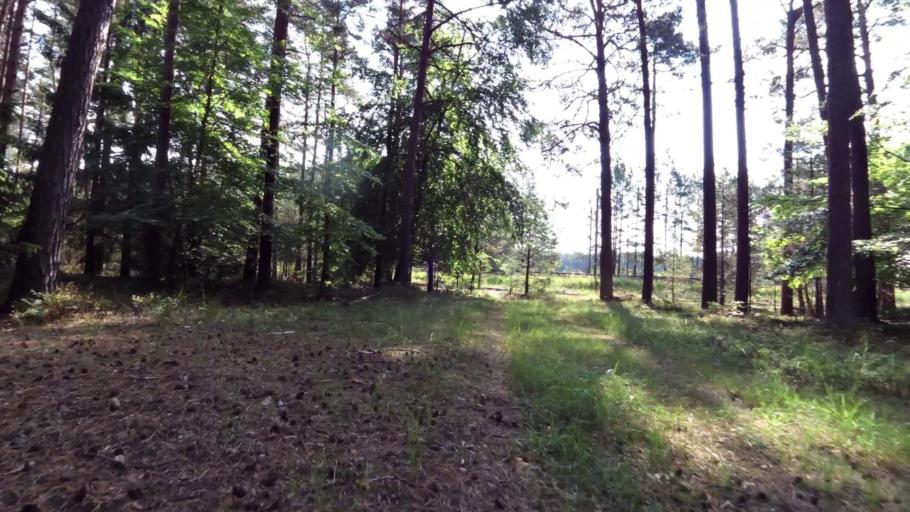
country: PL
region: West Pomeranian Voivodeship
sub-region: Powiat kamienski
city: Miedzyzdroje
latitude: 53.9240
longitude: 14.5095
